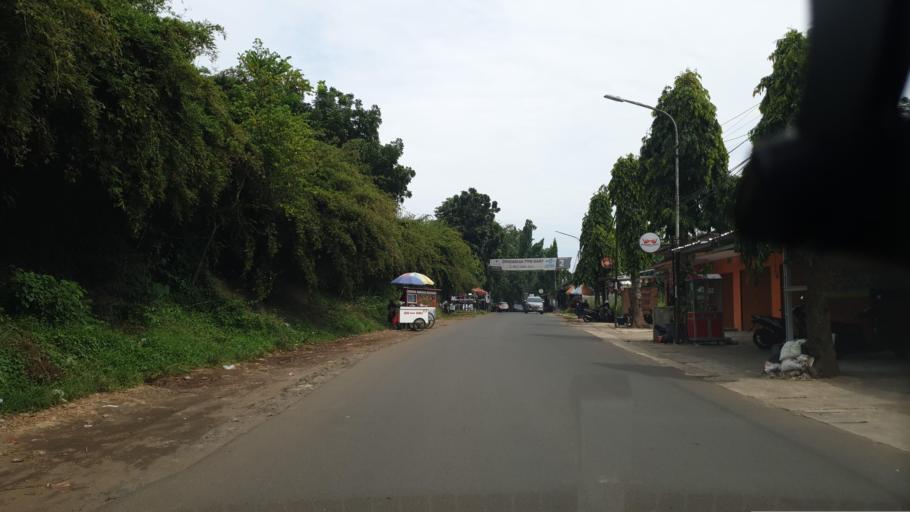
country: ID
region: West Java
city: Pamulang
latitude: -6.3506
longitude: 106.7649
